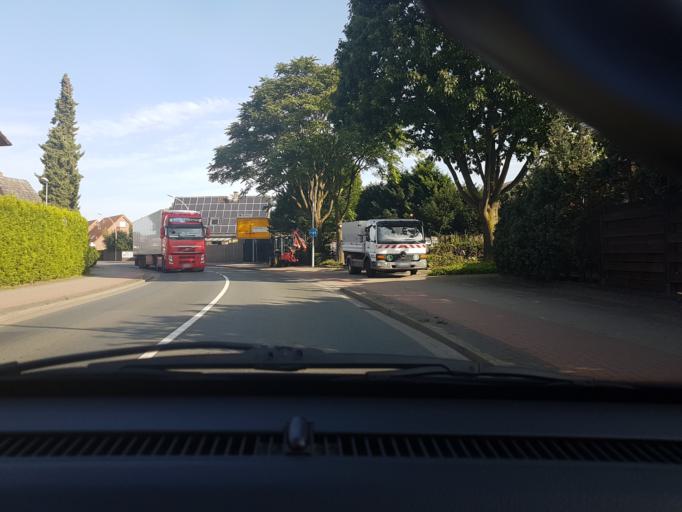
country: DE
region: North Rhine-Westphalia
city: Emsdetten
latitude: 52.1592
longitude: 7.5272
